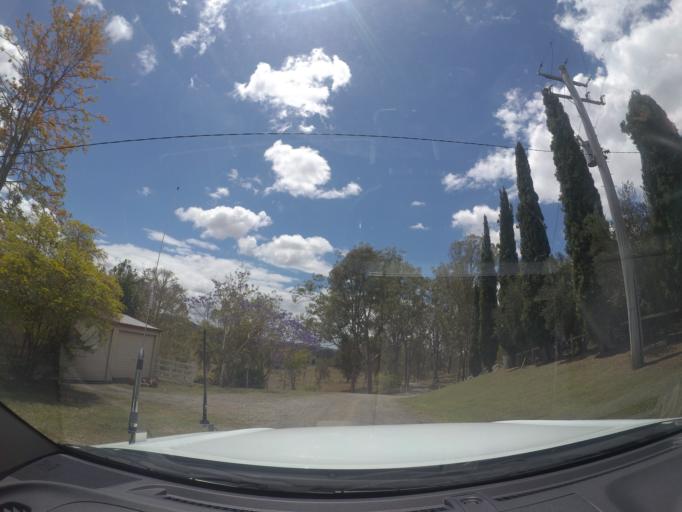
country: AU
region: Queensland
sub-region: Logan
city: Cedar Vale
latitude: -27.9045
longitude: 153.0583
